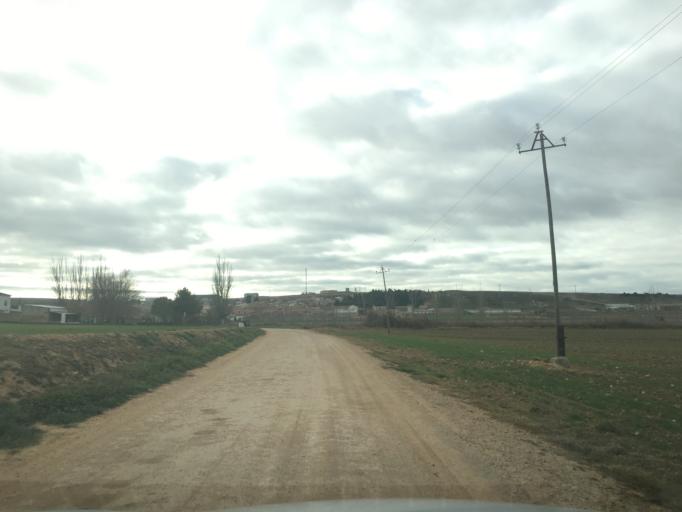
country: ES
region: Castille-La Mancha
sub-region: Provincia de Albacete
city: Petrola
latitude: 38.8330
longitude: -1.5581
